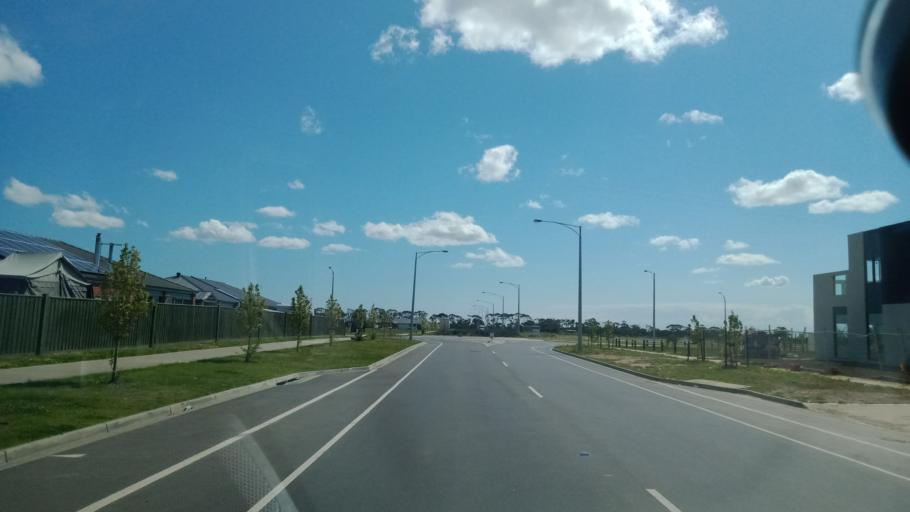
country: AU
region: Victoria
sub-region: Casey
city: Cranbourne West
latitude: -38.0938
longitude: 145.2507
